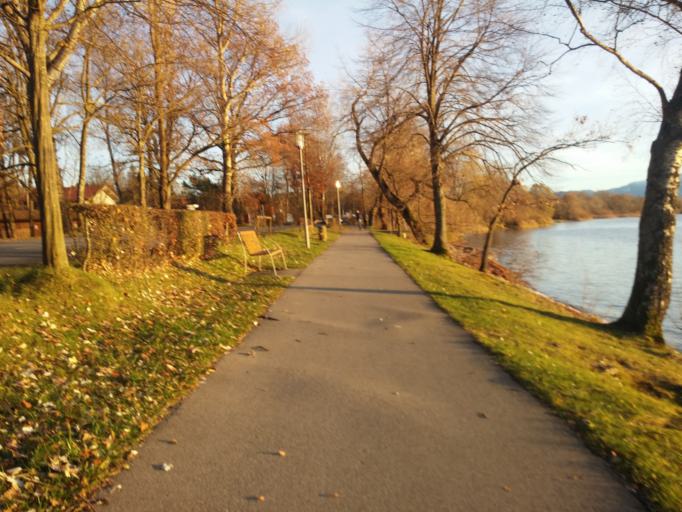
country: DE
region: Bavaria
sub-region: Upper Bavaria
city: Seeon-Seebruck
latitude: 47.9309
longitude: 12.4897
